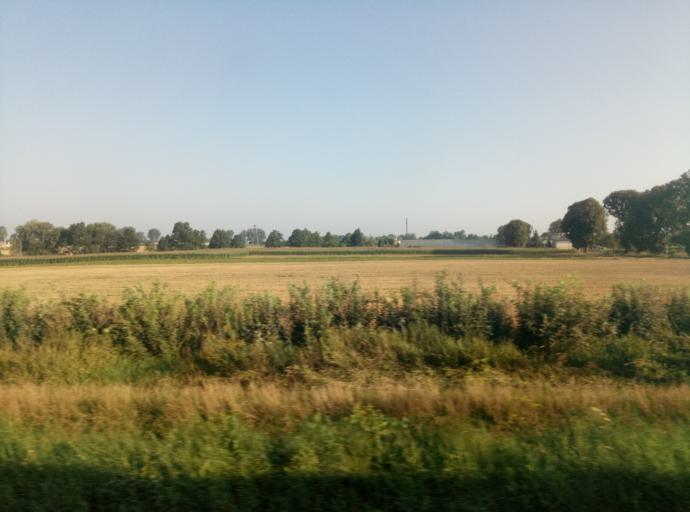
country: PL
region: Kujawsko-Pomorskie
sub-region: Powiat golubsko-dobrzynski
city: Kowalewo Pomorskie
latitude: 53.1400
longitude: 18.8086
